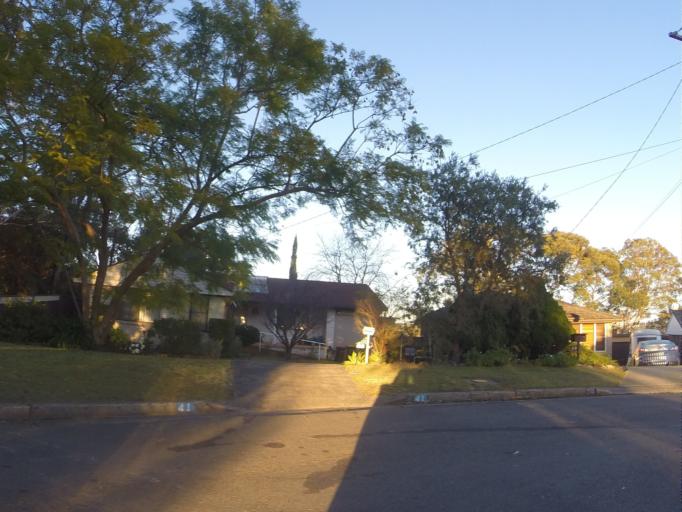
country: AU
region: New South Wales
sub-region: Sutherland Shire
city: Engadine
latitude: -34.0504
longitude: 151.0065
